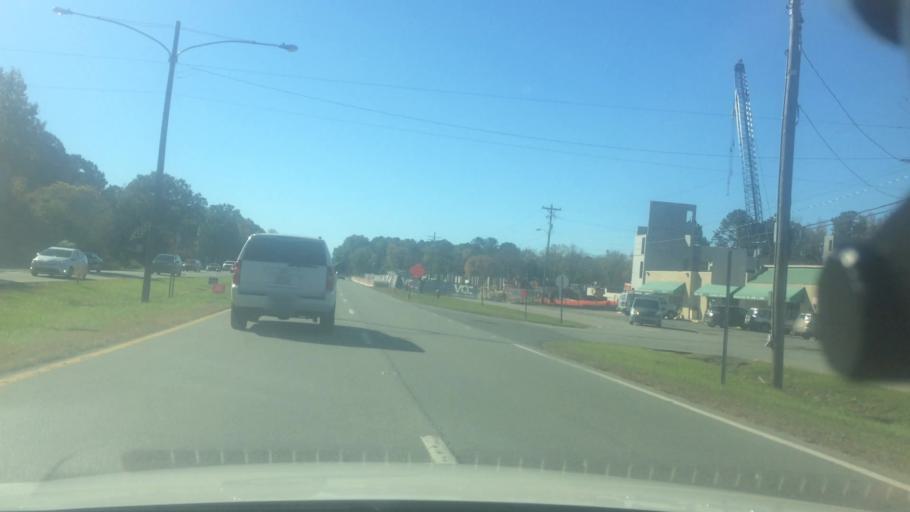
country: US
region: North Carolina
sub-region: Orange County
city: Chapel Hill
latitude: 35.9351
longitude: -79.0237
